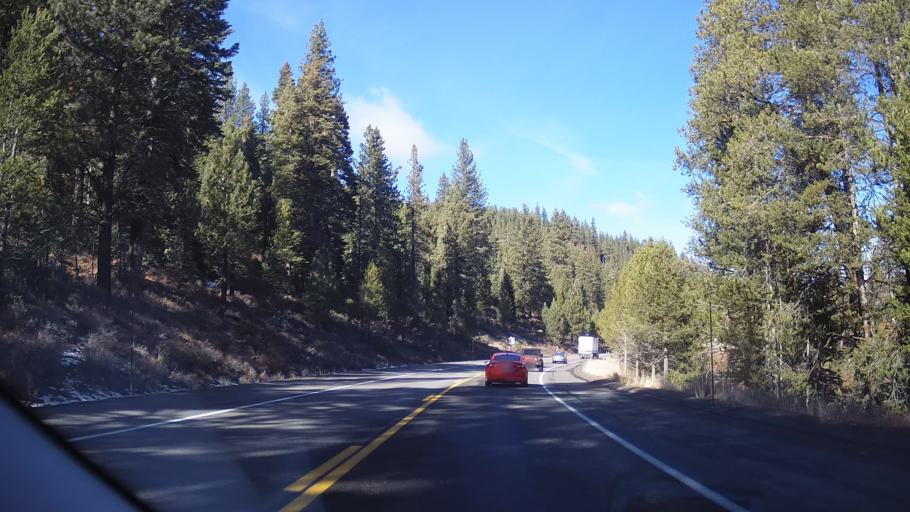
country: US
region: California
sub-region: Nevada County
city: Truckee
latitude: 39.2863
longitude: -120.2084
